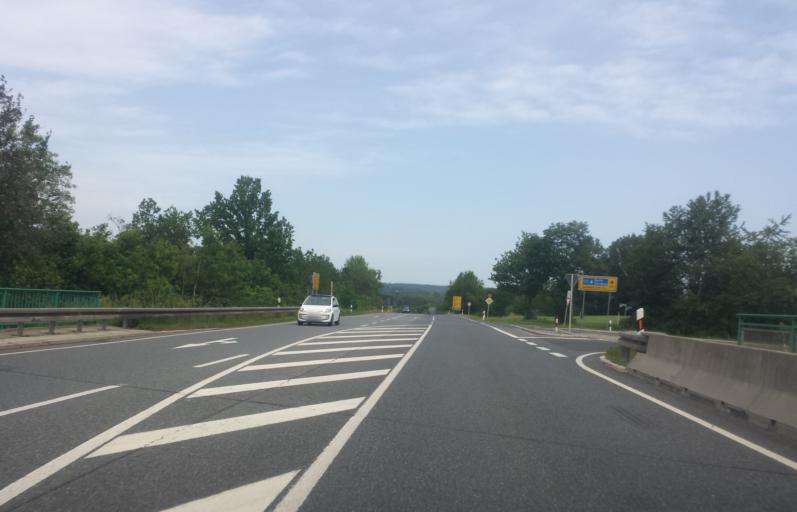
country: DE
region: Bavaria
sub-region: Upper Palatinate
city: Pressath
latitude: 49.7615
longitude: 11.9233
